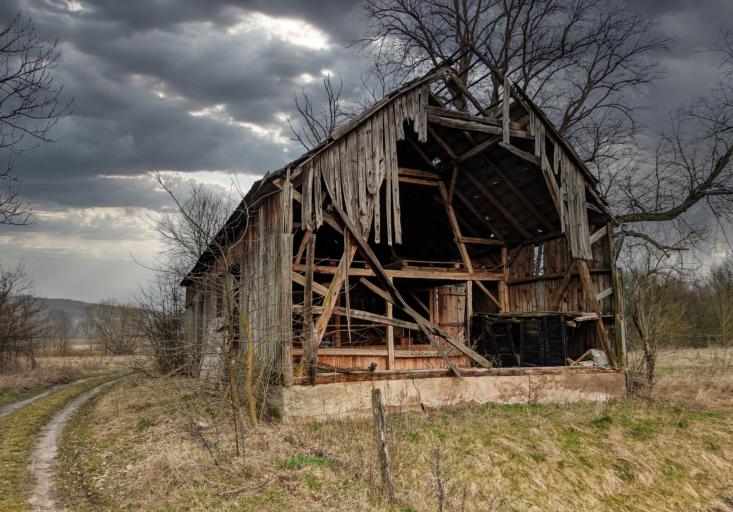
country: PL
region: Lubusz
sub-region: Powiat zielonogorski
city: Nowogrod Bobrzanski
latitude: 51.8450
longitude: 15.1985
